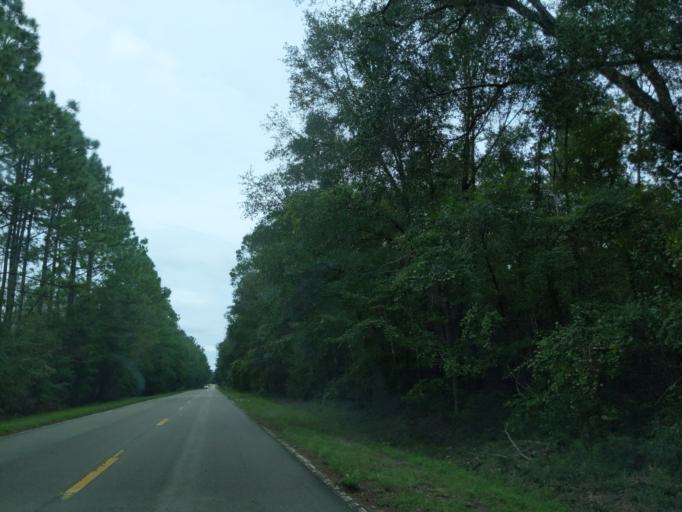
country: US
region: Florida
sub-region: Leon County
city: Woodville
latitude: 30.3725
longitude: -84.1469
